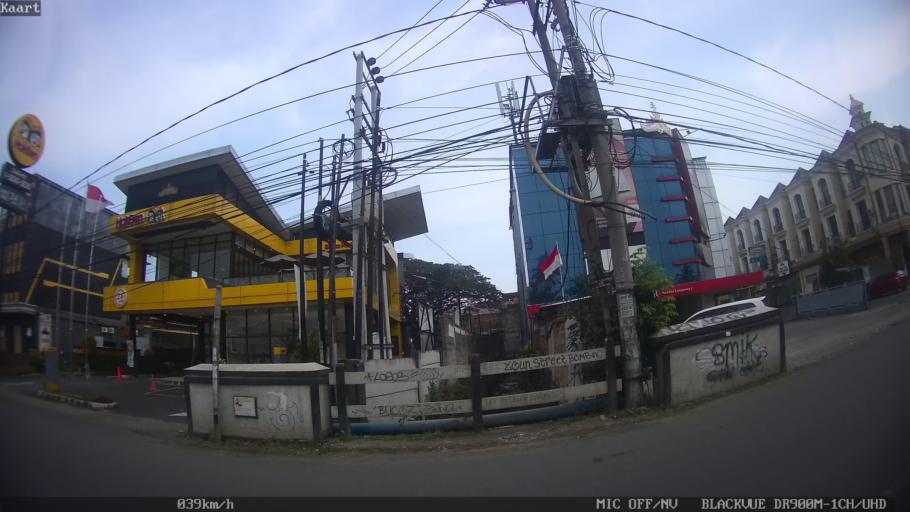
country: ID
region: Lampung
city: Bandarlampung
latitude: -5.4053
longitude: 105.2759
